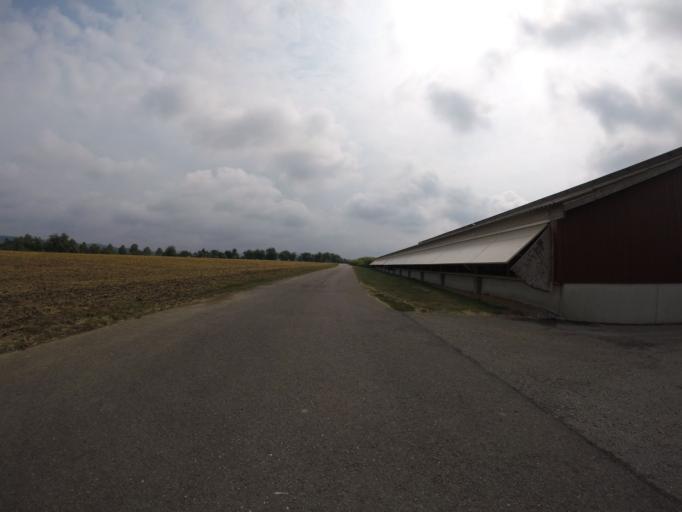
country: DE
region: Baden-Wuerttemberg
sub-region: Regierungsbezirk Stuttgart
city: Aspach
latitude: 48.9585
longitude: 9.4040
